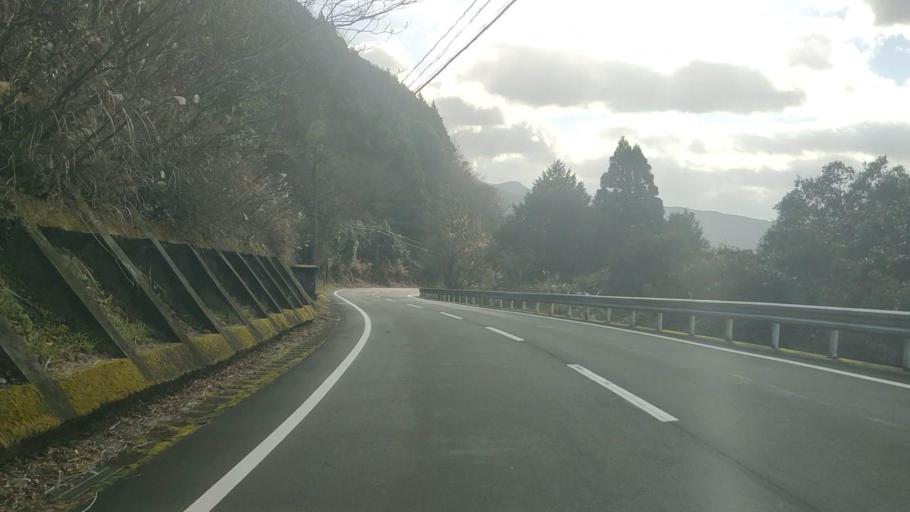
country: JP
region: Kumamoto
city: Hitoyoshi
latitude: 32.3209
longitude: 130.8408
